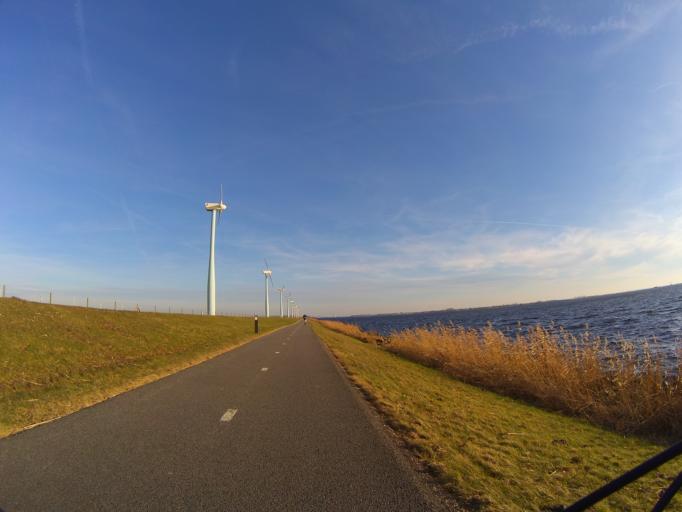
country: NL
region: Utrecht
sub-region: Gemeente Bunschoten
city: Spakenburg
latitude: 52.2830
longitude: 5.3532
